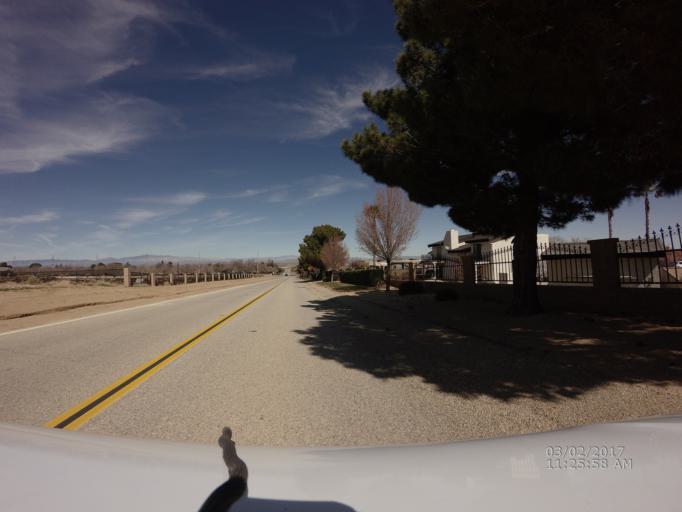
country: US
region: California
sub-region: Los Angeles County
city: Quartz Hill
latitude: 34.6435
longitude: -118.2448
